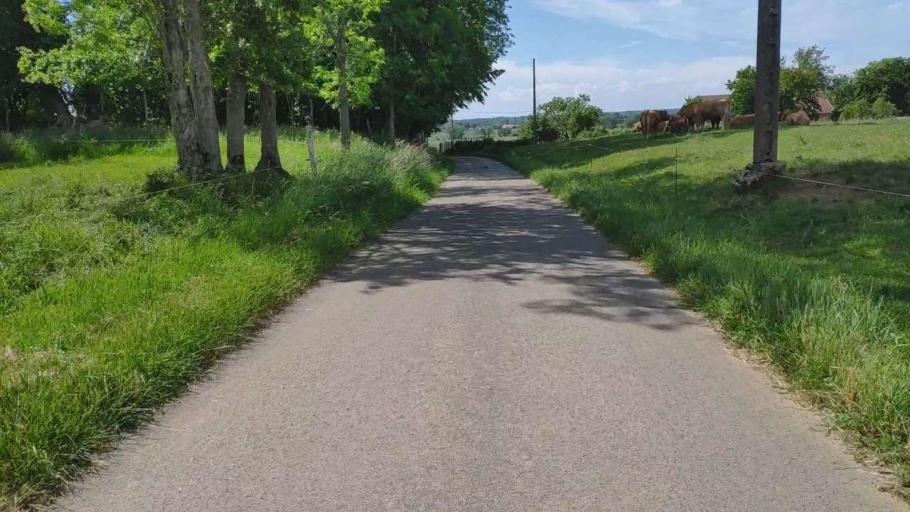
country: FR
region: Franche-Comte
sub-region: Departement du Jura
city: Bletterans
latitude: 46.7316
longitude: 5.5030
